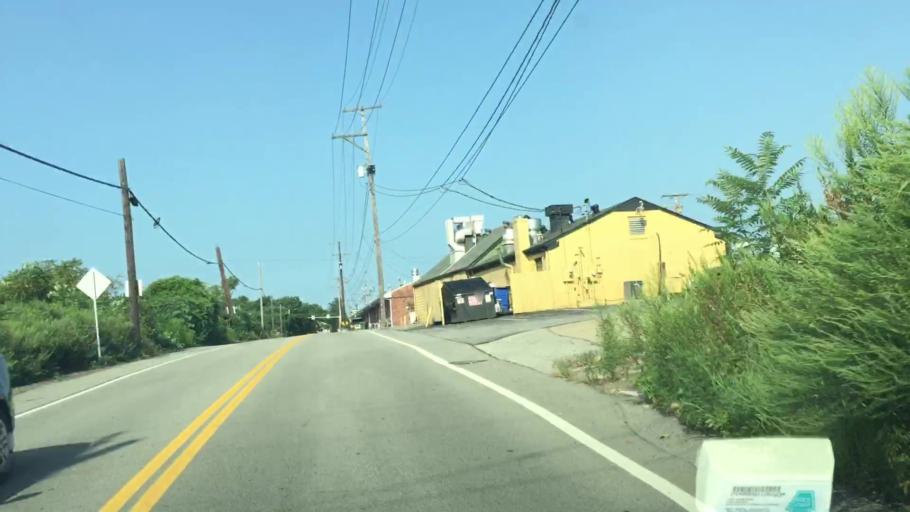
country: US
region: Pennsylvania
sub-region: Allegheny County
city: Blawnox
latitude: 40.4876
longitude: -79.8800
